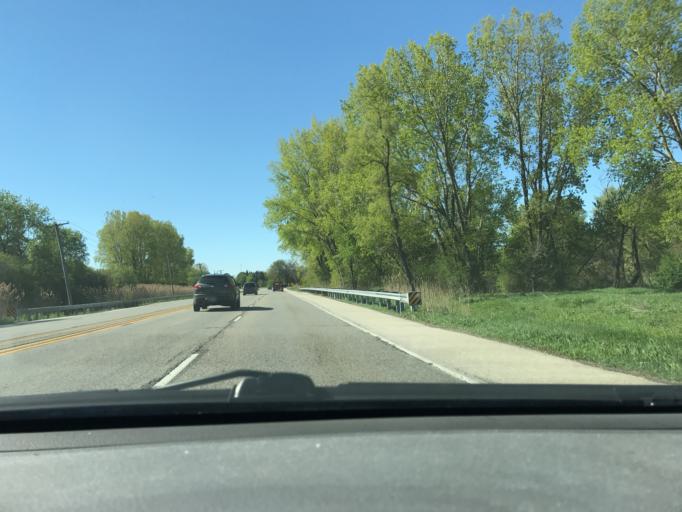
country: US
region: Illinois
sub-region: Kane County
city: Elgin
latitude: 42.0403
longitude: -88.3412
